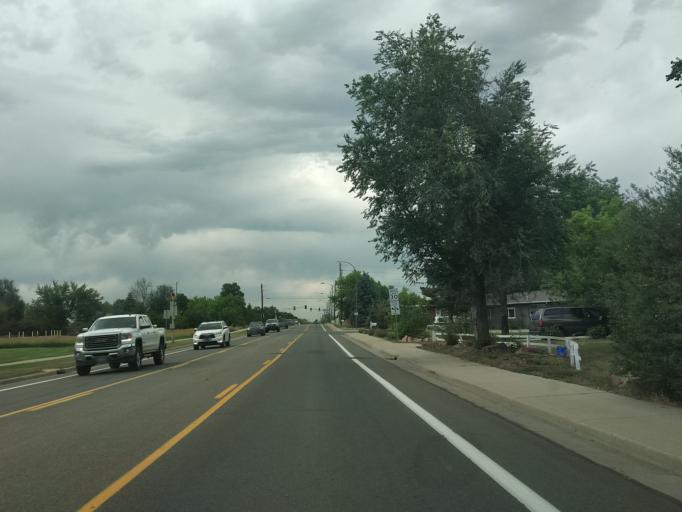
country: US
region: Colorado
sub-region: Jefferson County
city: Lakewood
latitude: 39.7024
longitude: -105.1002
